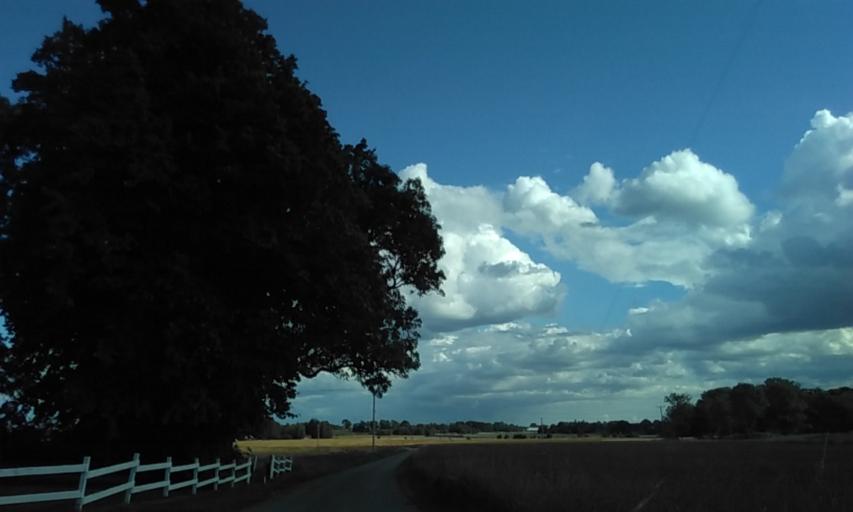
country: SE
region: Vaestra Goetaland
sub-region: Lidkopings Kommun
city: Lidkoping
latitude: 58.5779
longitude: 13.0136
